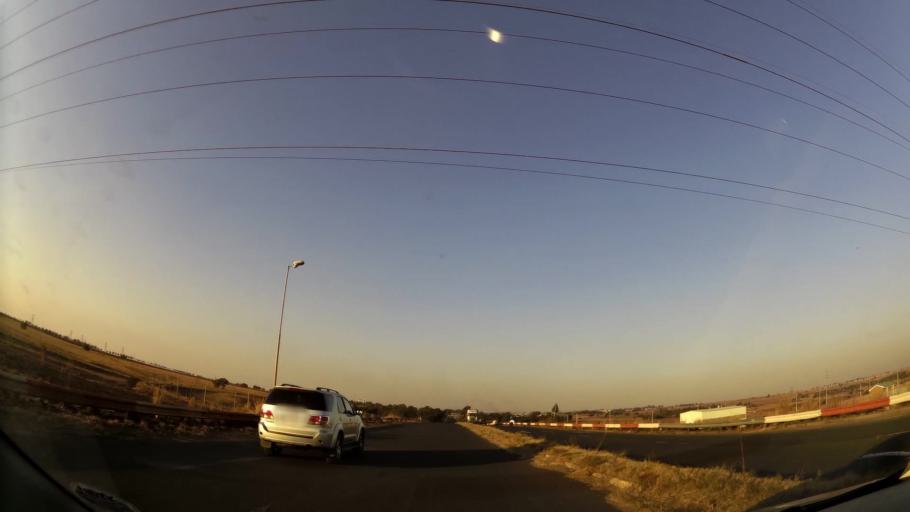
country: ZA
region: Gauteng
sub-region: West Rand District Municipality
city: Randfontein
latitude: -26.2052
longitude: 27.6628
